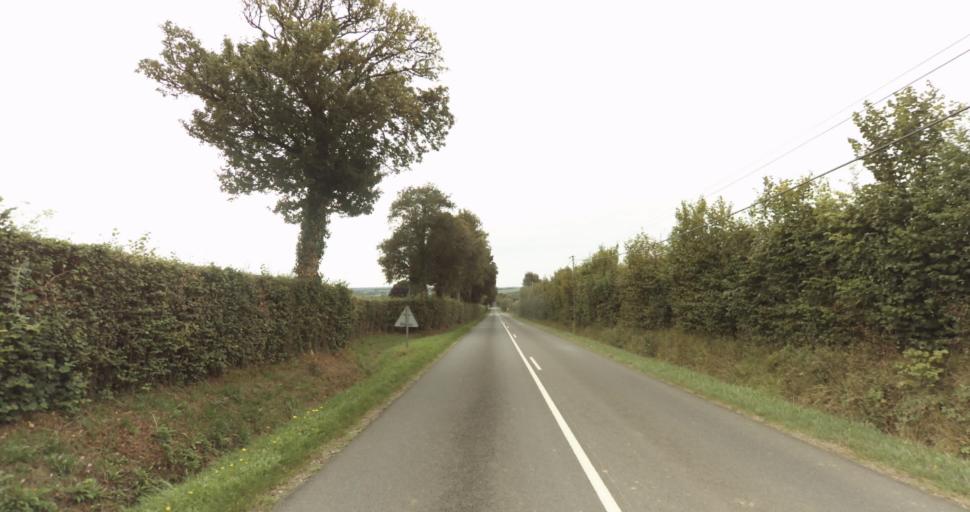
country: FR
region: Lower Normandy
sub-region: Departement de l'Orne
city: Gace
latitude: 48.6840
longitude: 0.2895
